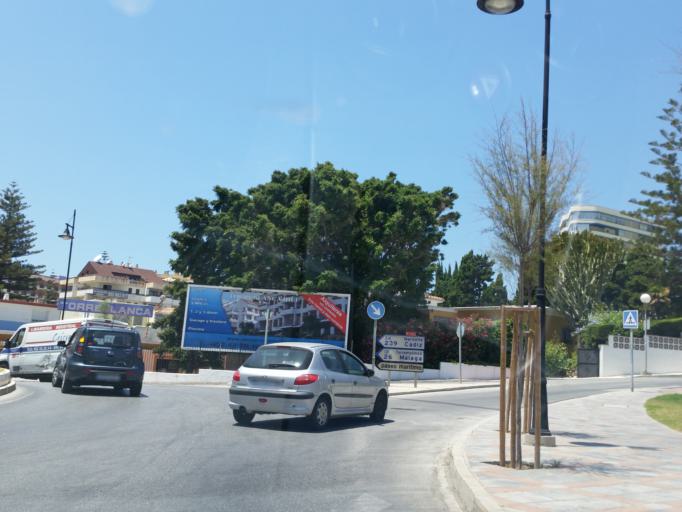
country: ES
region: Andalusia
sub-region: Provincia de Malaga
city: Fuengirola
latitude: 36.5638
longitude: -4.6045
